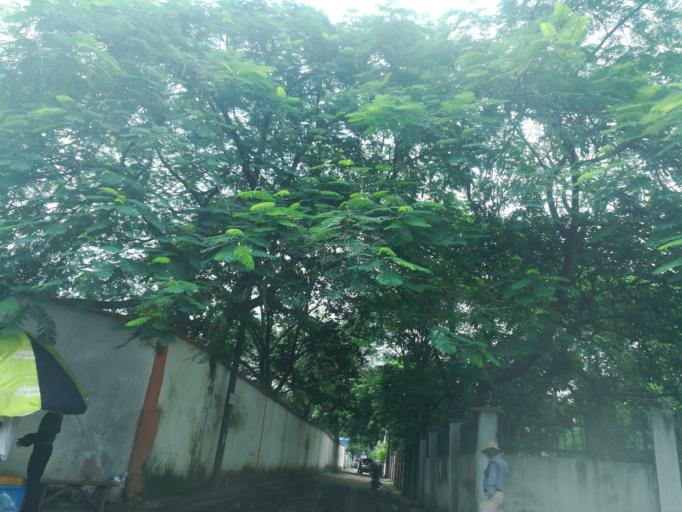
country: NG
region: Lagos
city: Ojota
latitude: 6.5680
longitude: 3.3660
